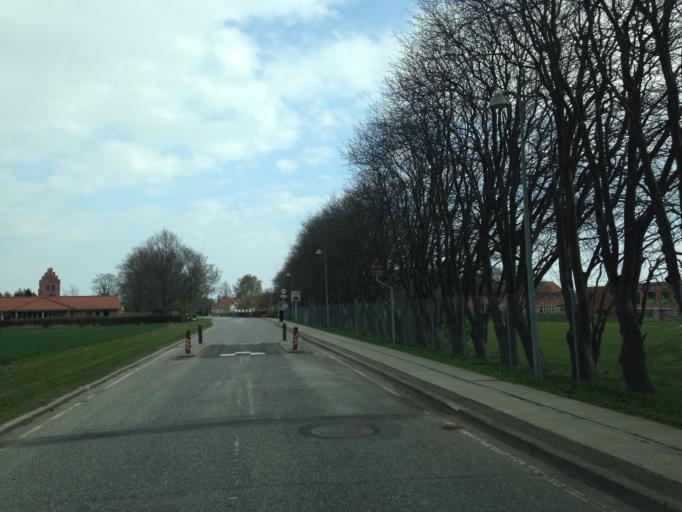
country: DK
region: Capital Region
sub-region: Hoje-Taastrup Kommune
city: Taastrup
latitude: 55.6268
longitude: 12.2948
